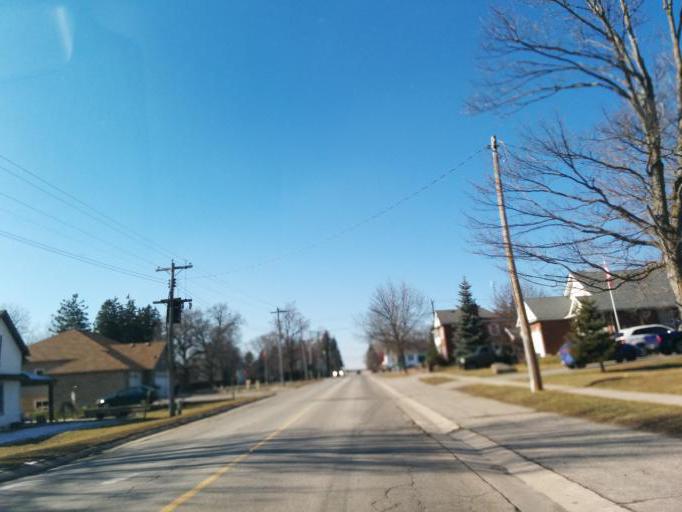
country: CA
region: Ontario
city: Brant
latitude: 43.0321
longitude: -80.3295
